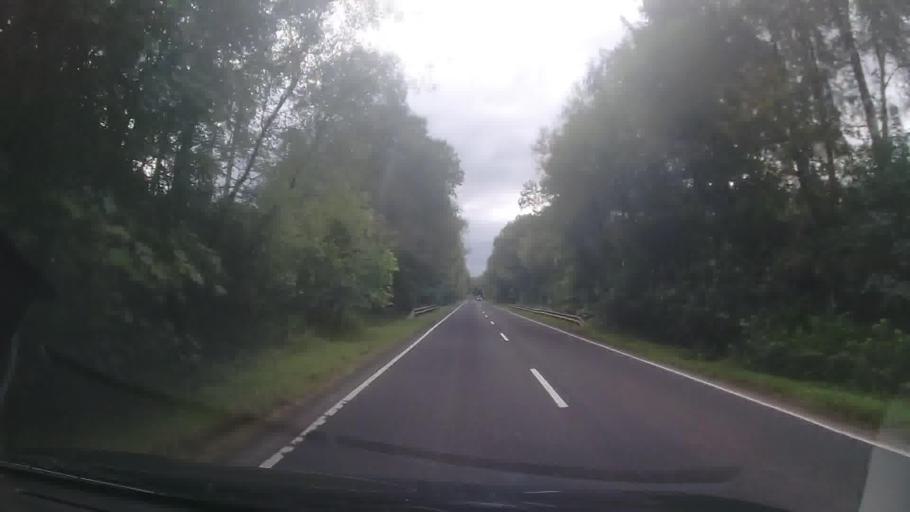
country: GB
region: Scotland
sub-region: Argyll and Bute
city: Garelochhead
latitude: 56.2442
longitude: -4.9471
